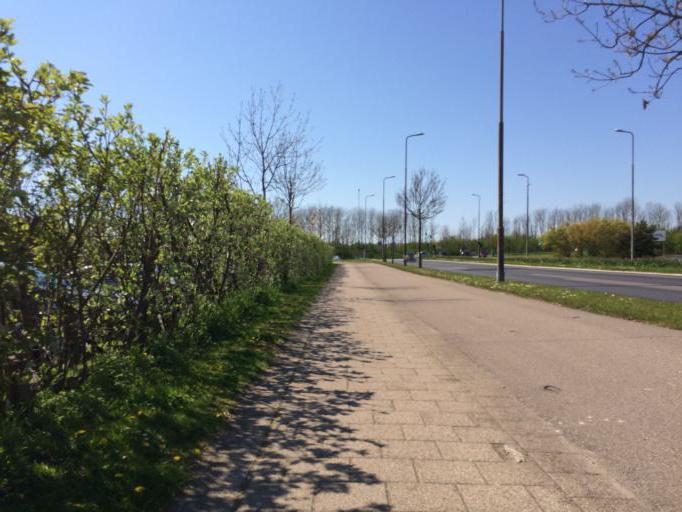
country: DK
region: Capital Region
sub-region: Hoje-Taastrup Kommune
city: Taastrup
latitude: 55.6468
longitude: 12.2840
